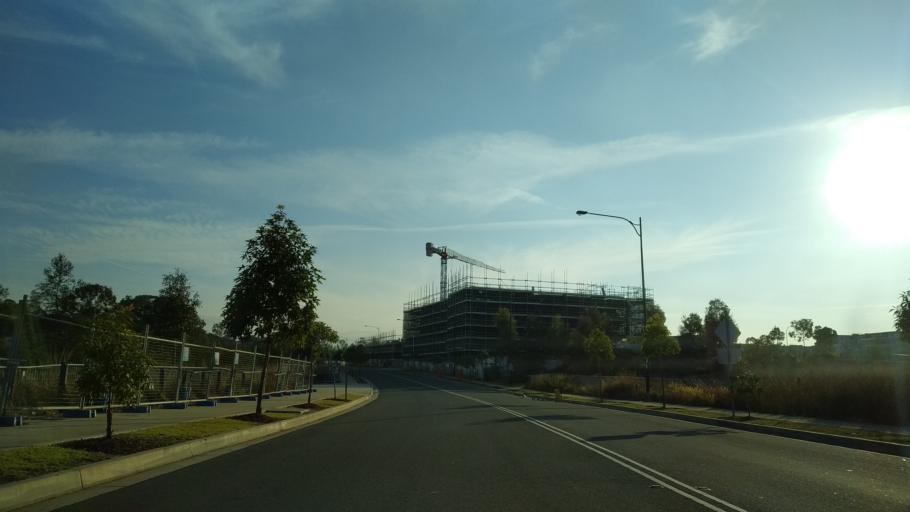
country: AU
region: New South Wales
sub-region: Penrith Municipality
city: Werrington Downs
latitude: -33.7284
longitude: 150.7303
